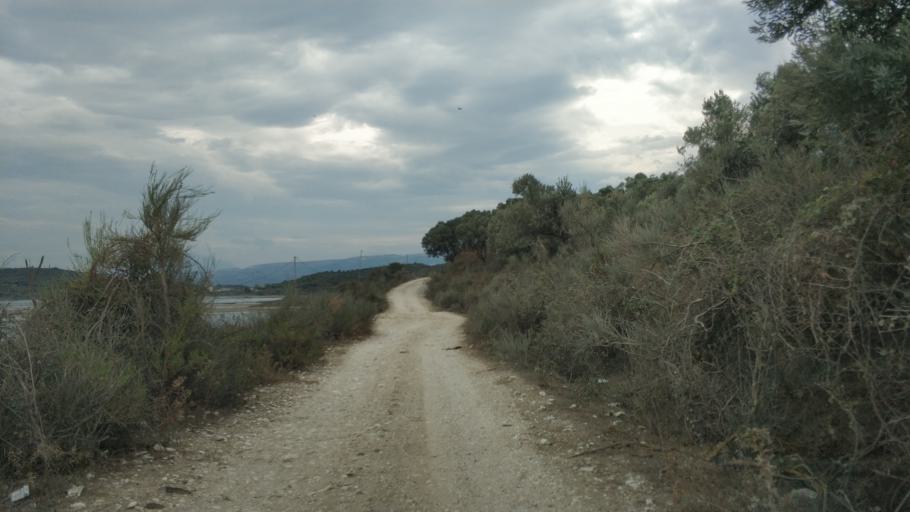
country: AL
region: Vlore
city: Vlore
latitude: 40.5175
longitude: 19.3931
